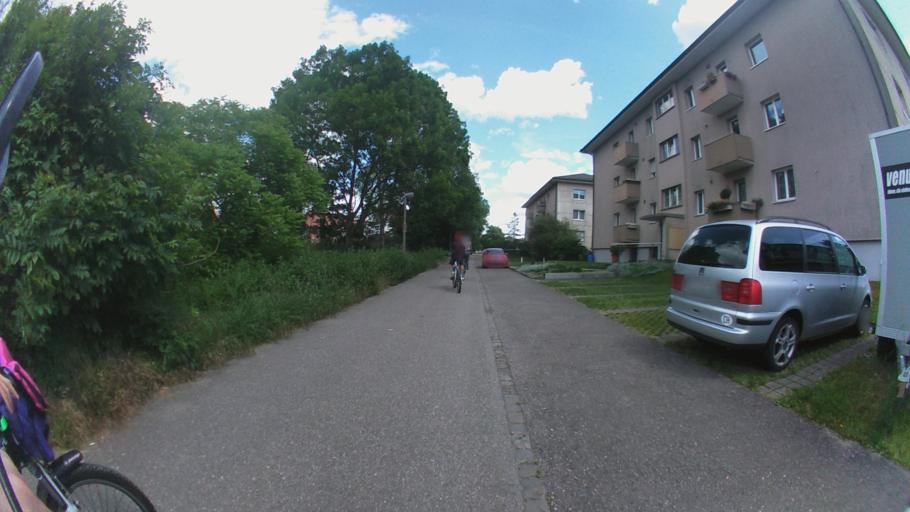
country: CH
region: Zurich
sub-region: Bezirk Dielsdorf
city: Regensdorf
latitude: 47.4426
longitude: 8.4776
